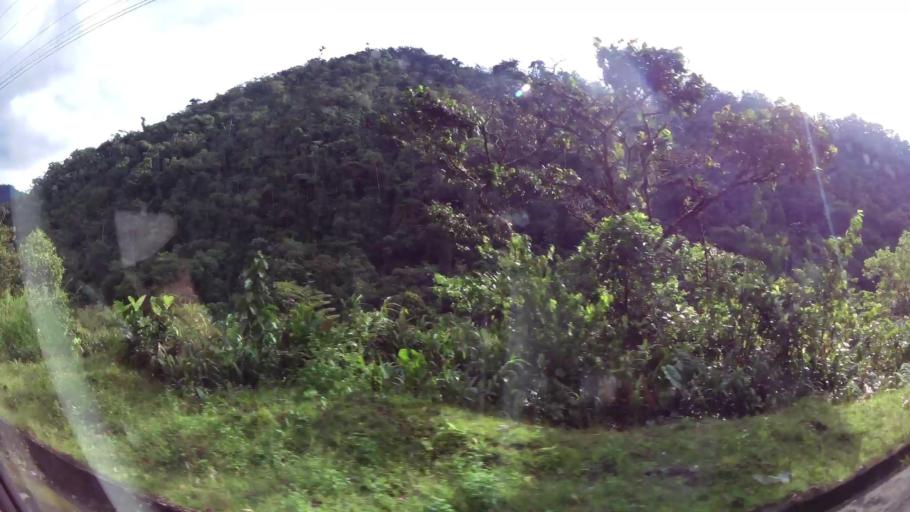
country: EC
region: Pastaza
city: Puyo
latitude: -1.4127
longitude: -78.1849
